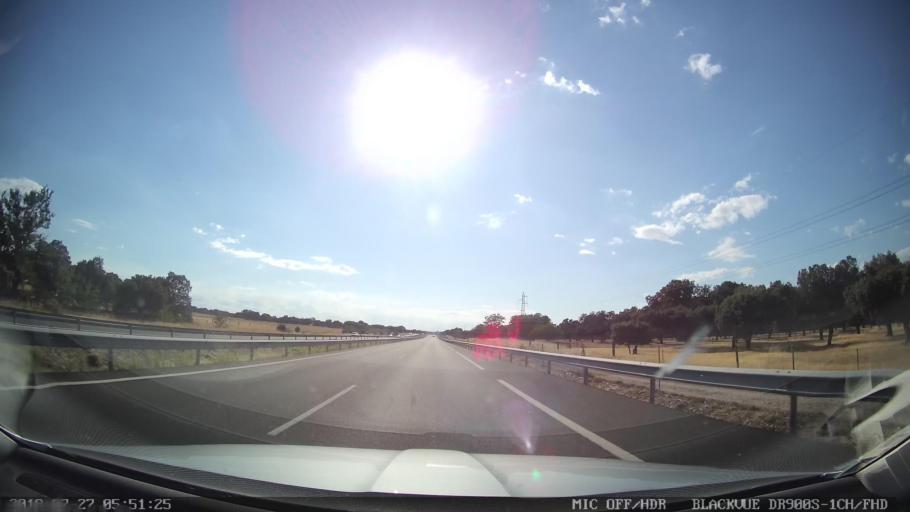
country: ES
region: Castille-La Mancha
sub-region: Province of Toledo
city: Alcanizo
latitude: 39.9253
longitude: -5.0967
